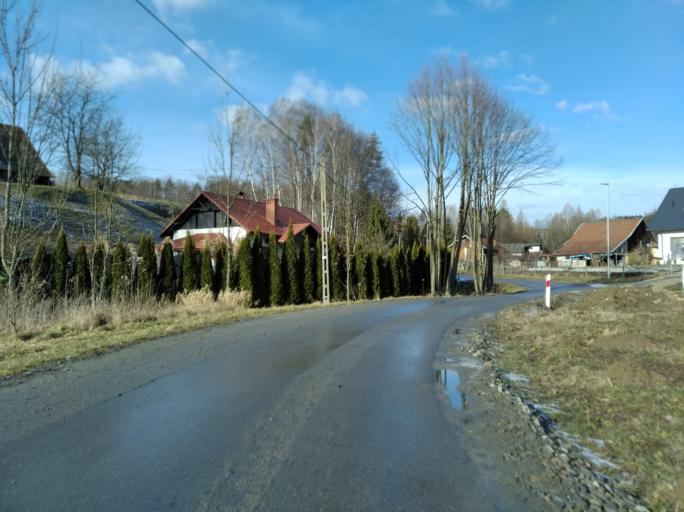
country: PL
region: Subcarpathian Voivodeship
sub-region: Powiat strzyzowski
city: Strzyzow
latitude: 49.8952
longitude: 21.7764
